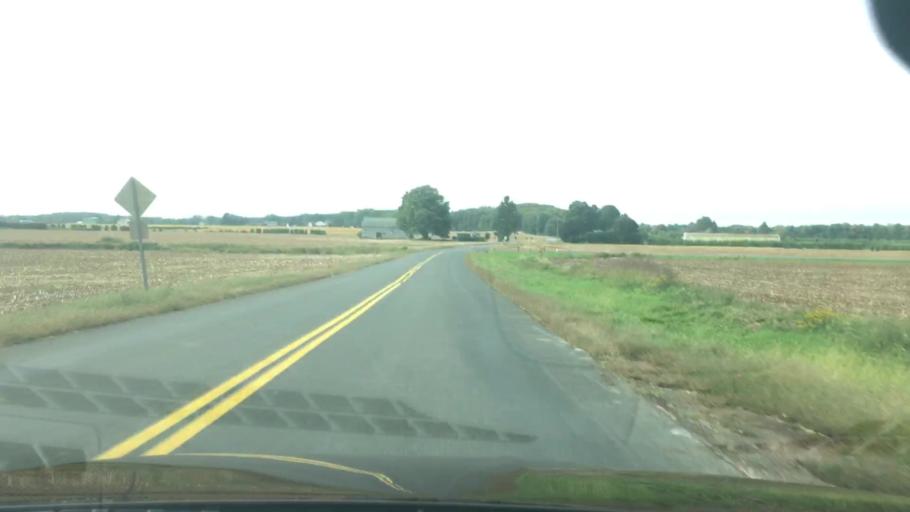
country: US
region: Connecticut
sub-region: Hartford County
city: Broad Brook
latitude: 41.8997
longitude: -72.5086
